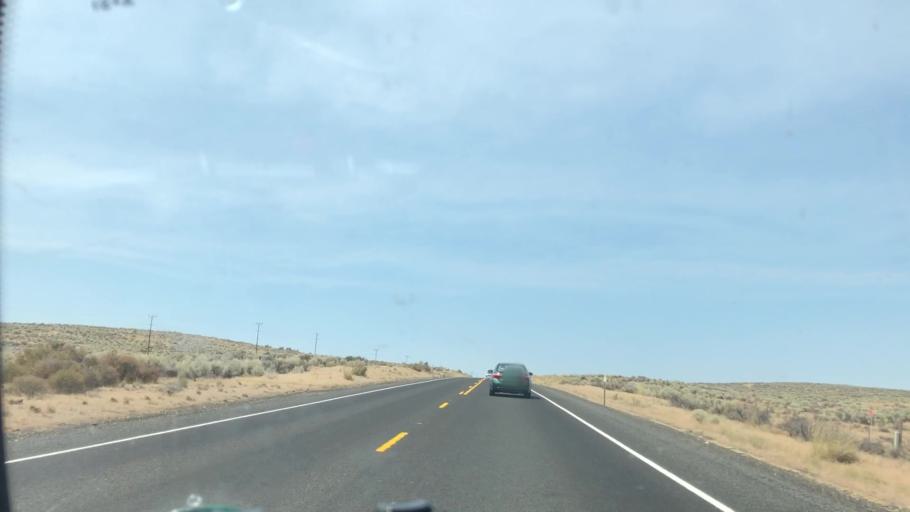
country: US
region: Idaho
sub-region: Owyhee County
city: Murphy
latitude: 42.9899
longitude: -117.0575
